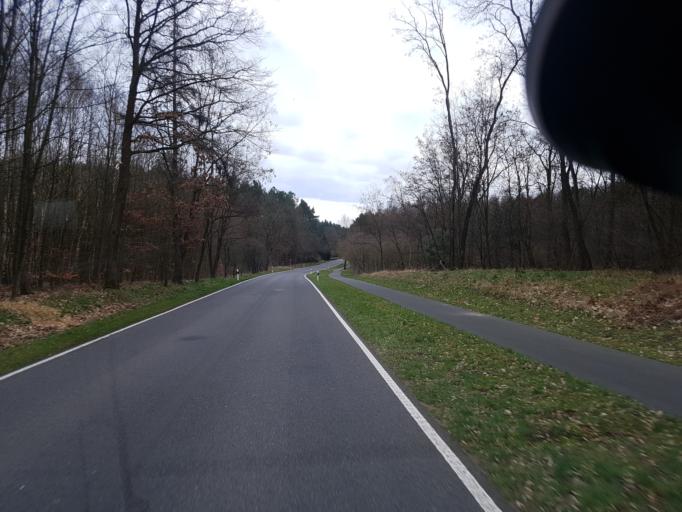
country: DE
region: Brandenburg
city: Gross Lindow
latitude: 52.1667
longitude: 14.4992
